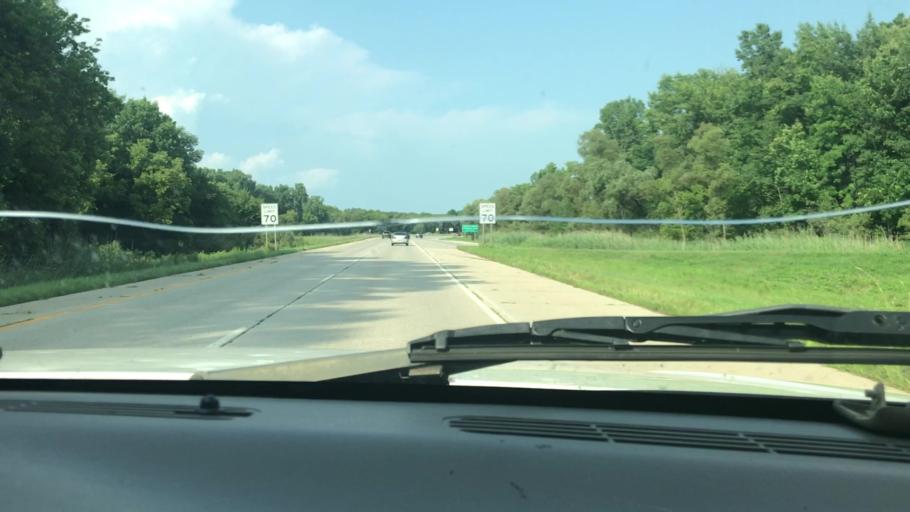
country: US
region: Wisconsin
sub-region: Brown County
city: Green Bay
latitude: 44.5213
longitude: -87.9503
